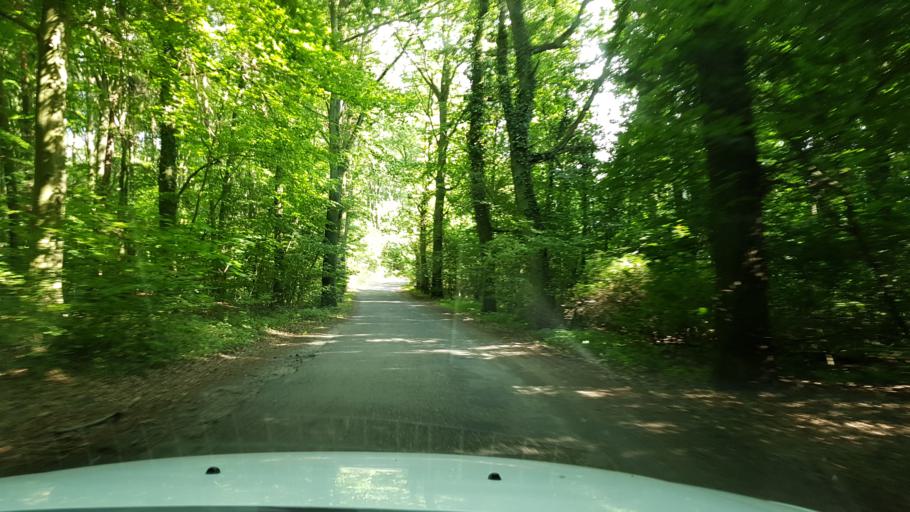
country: PL
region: West Pomeranian Voivodeship
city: Trzcinsko Zdroj
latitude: 52.9448
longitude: 14.5497
